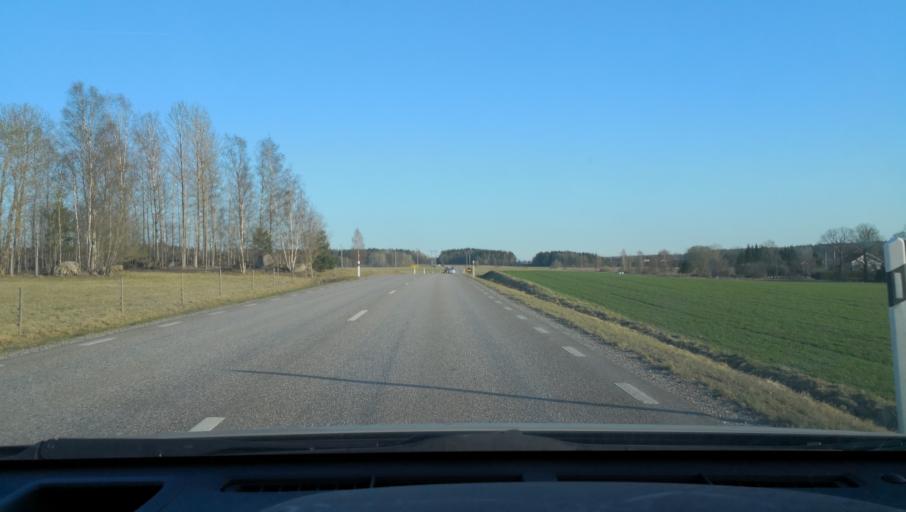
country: SE
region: Uppsala
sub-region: Heby Kommun
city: Heby
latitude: 59.9242
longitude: 16.8795
